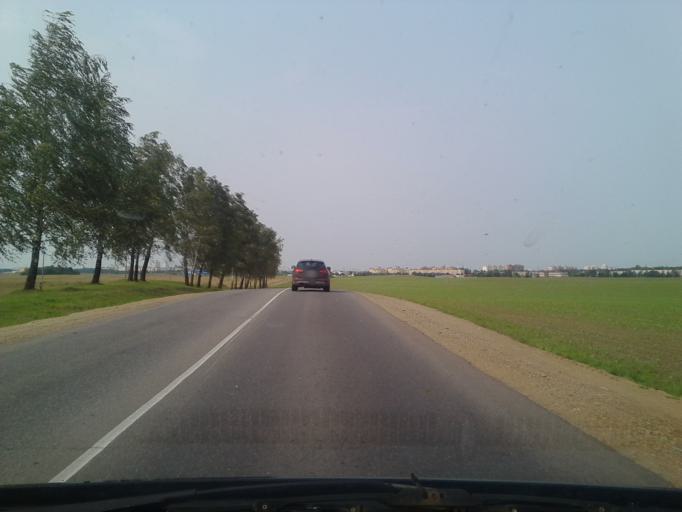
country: BY
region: Minsk
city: Hatava
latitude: 53.8243
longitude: 27.6282
